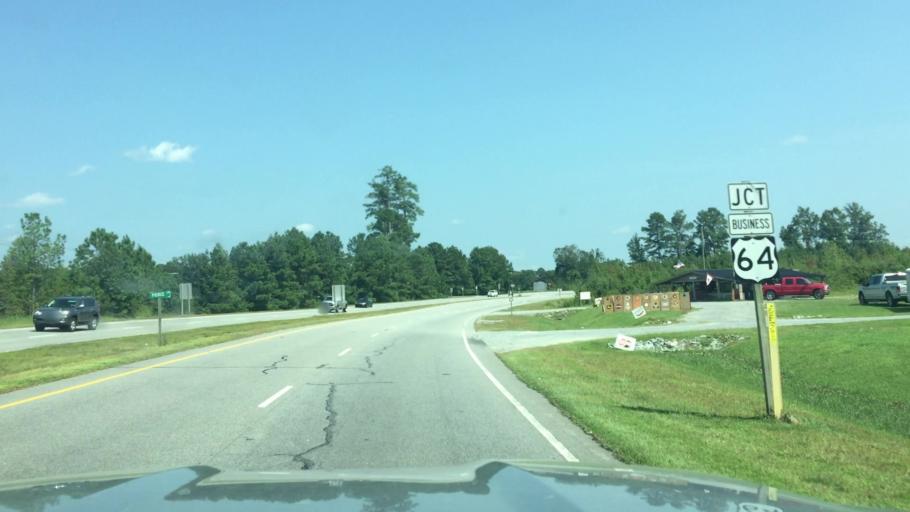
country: US
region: North Carolina
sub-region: Martin County
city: Williamston
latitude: 35.8126
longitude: -76.9178
